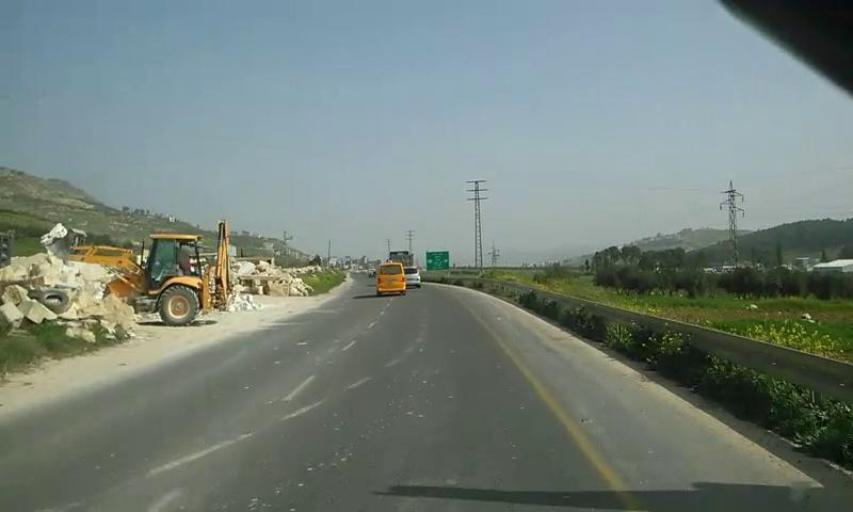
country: PS
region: West Bank
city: `Awarta
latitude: 32.1730
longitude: 35.2707
